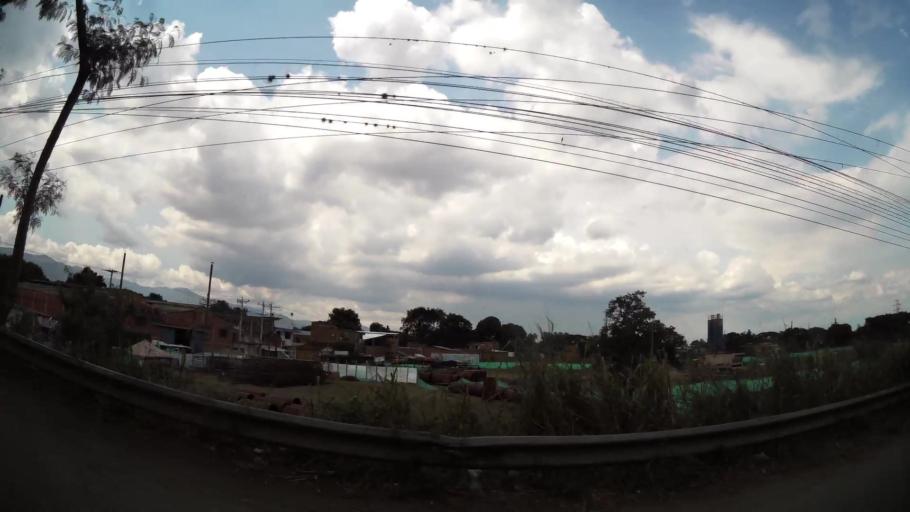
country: CO
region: Valle del Cauca
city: Cali
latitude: 3.4506
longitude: -76.4749
